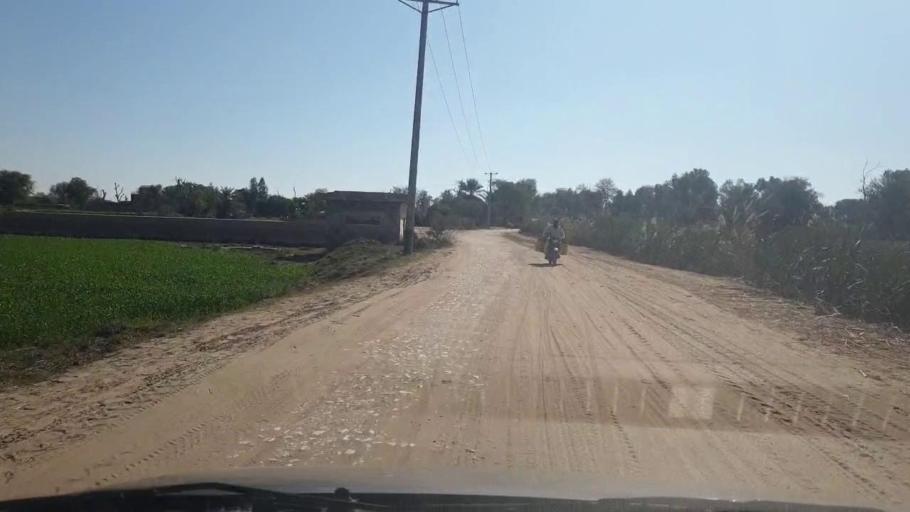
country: PK
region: Sindh
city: Bozdar
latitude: 27.0720
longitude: 68.6185
